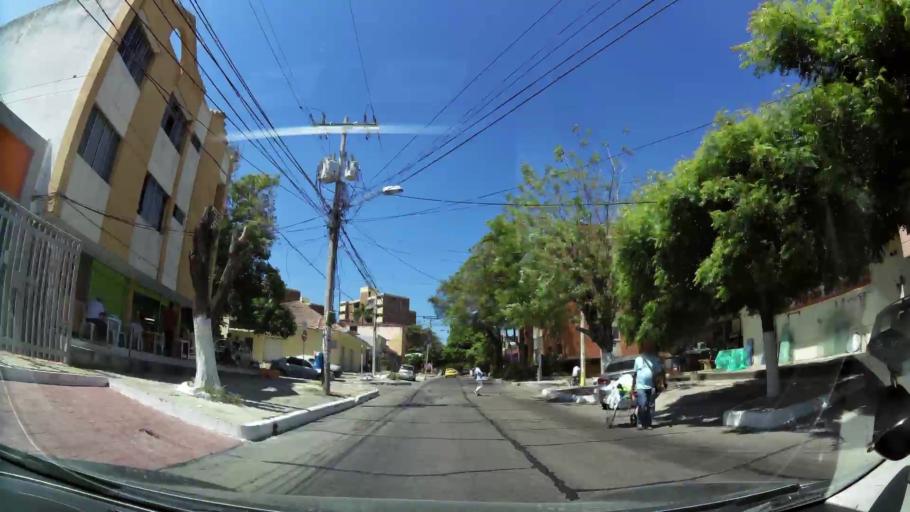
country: CO
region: Atlantico
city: Barranquilla
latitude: 10.9912
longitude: -74.8022
